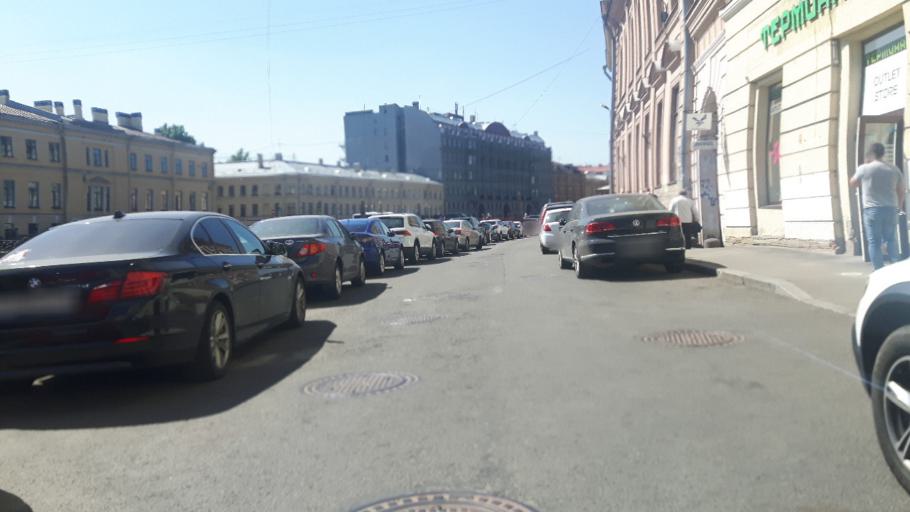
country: RU
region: St.-Petersburg
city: Saint Petersburg
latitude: 59.9338
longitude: 30.3166
